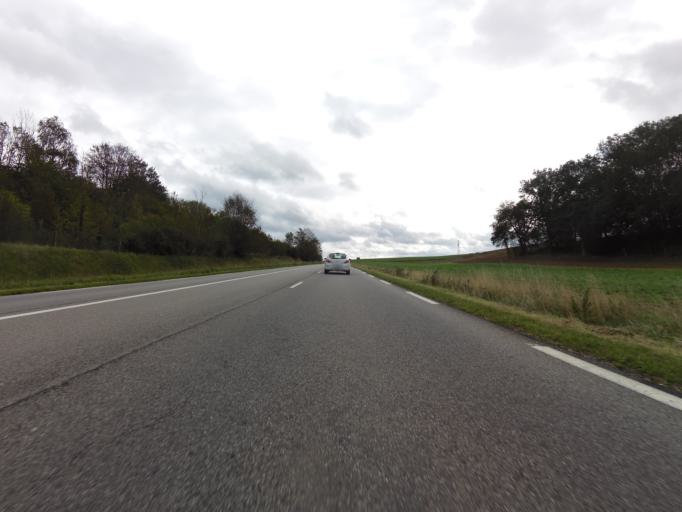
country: FR
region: Haute-Normandie
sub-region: Departement de la Seine-Maritime
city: Criel-sur-Mer
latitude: 50.0215
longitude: 1.3483
